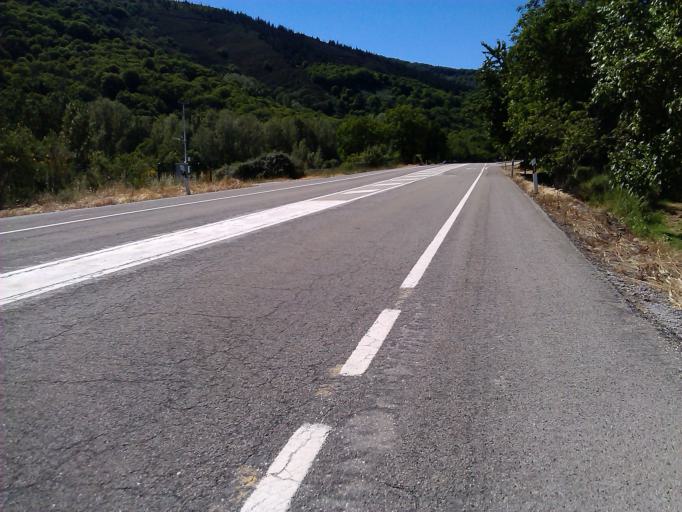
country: ES
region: Castille and Leon
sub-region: Provincia de Leon
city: Villafranca del Bierzo
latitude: 42.6245
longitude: -6.8424
